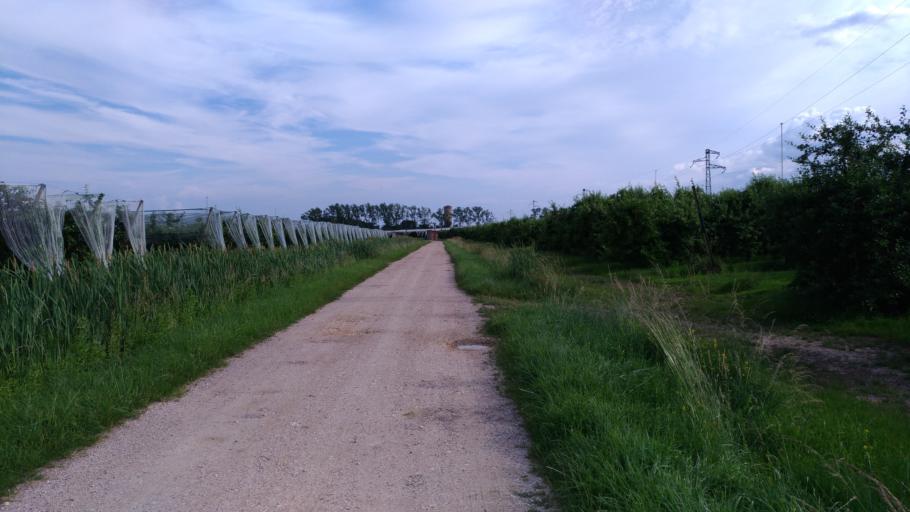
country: FR
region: Midi-Pyrenees
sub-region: Departement du Tarn-et-Garonne
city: Bressols
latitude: 43.9563
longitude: 1.3226
